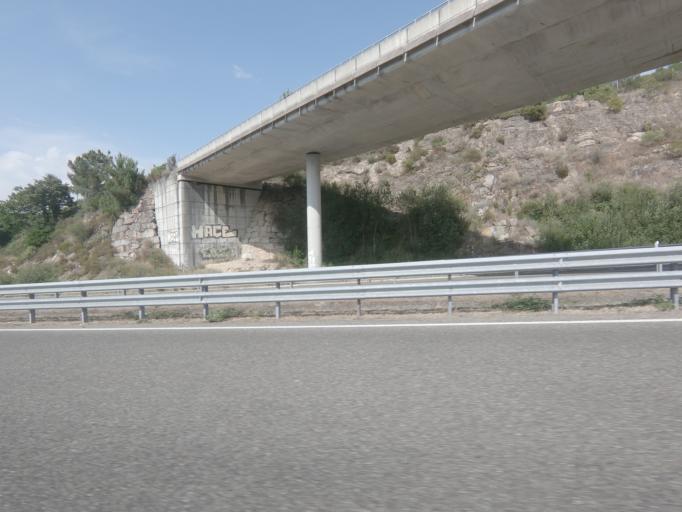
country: ES
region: Galicia
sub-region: Provincia de Ourense
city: Ourense
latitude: 42.2836
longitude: -7.8741
